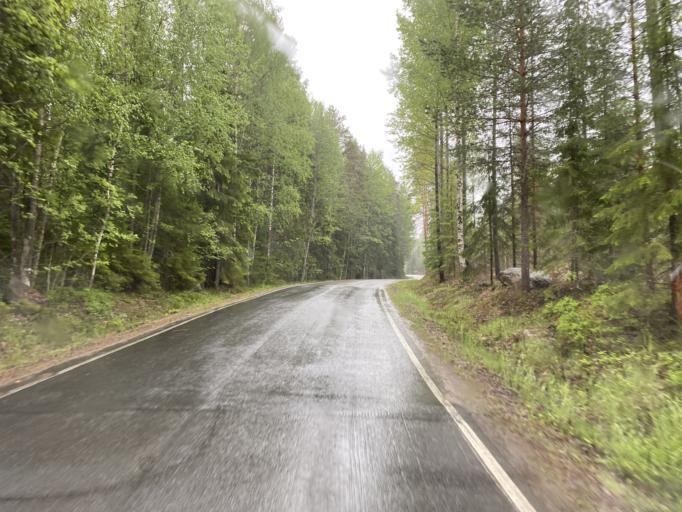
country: FI
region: Haeme
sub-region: Forssa
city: Humppila
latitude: 61.0883
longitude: 23.3090
